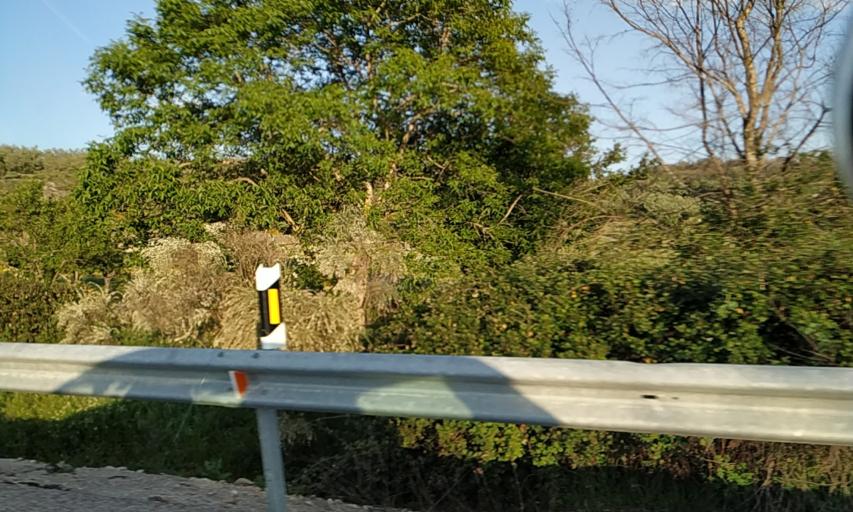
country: ES
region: Extremadura
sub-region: Provincia de Caceres
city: Valencia de Alcantara
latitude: 39.3772
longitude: -7.2536
